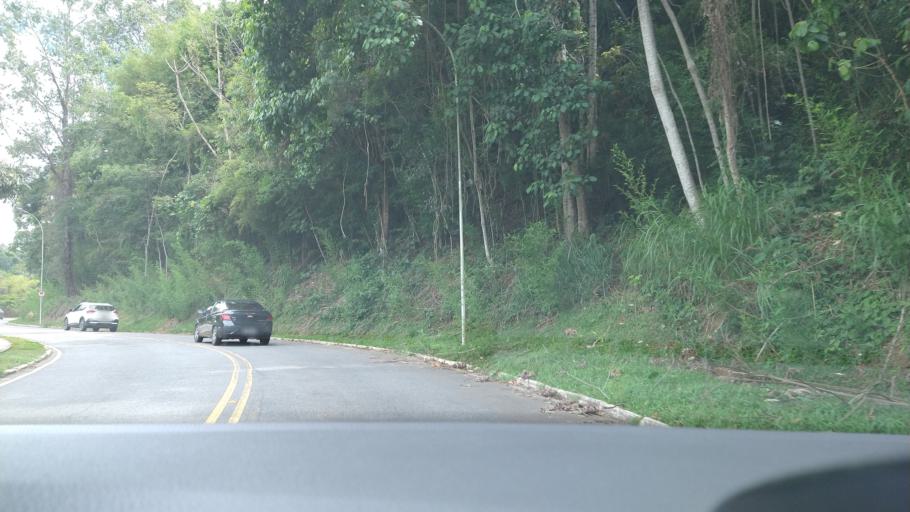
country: BR
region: Minas Gerais
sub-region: Vicosa
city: Vicosa
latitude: -20.7625
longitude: -42.8716
